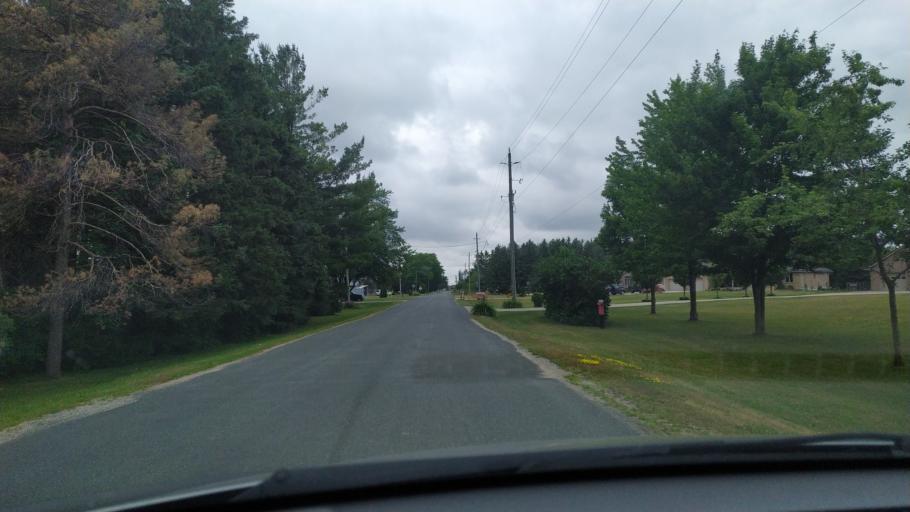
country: CA
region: Ontario
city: Stratford
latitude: 43.3669
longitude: -80.9309
